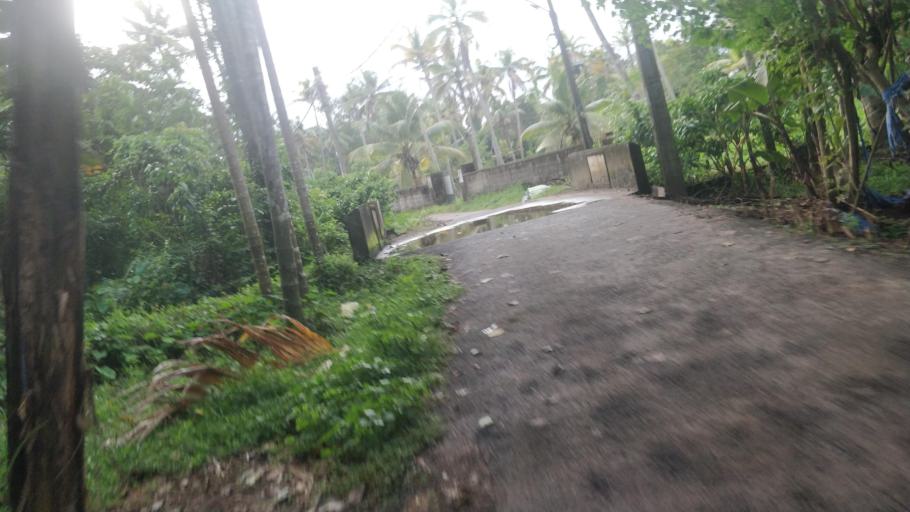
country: IN
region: Kerala
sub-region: Alappuzha
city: Shertallai
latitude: 9.6887
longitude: 76.3474
